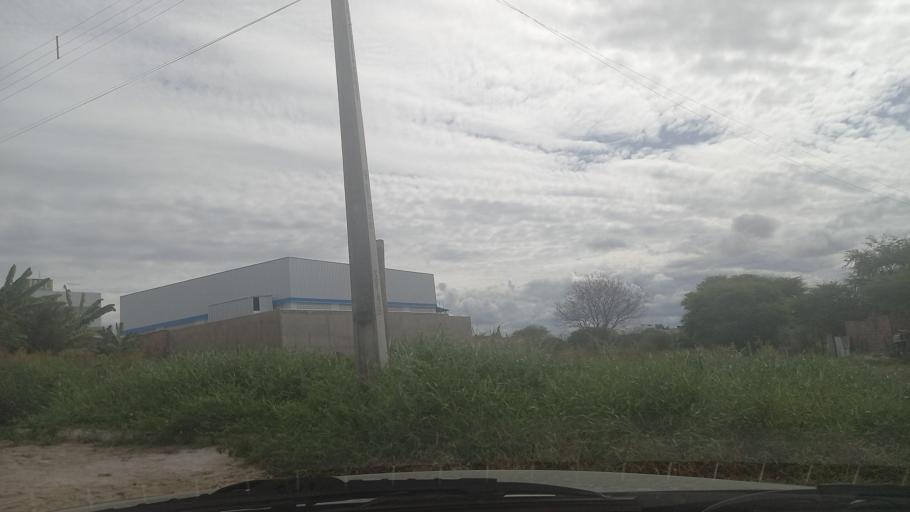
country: BR
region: Pernambuco
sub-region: Caruaru
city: Caruaru
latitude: -8.2902
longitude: -35.9897
